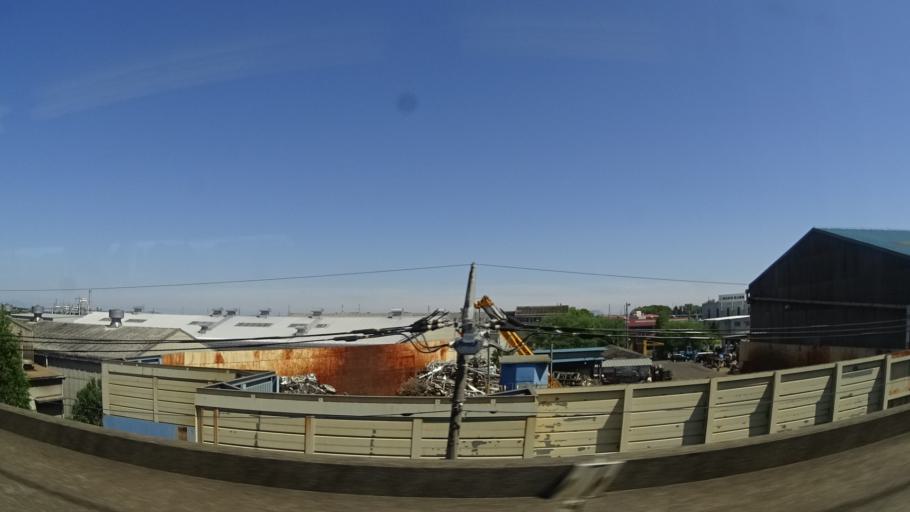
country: JP
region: Saitama
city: Kukichuo
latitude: 36.0835
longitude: 139.6890
